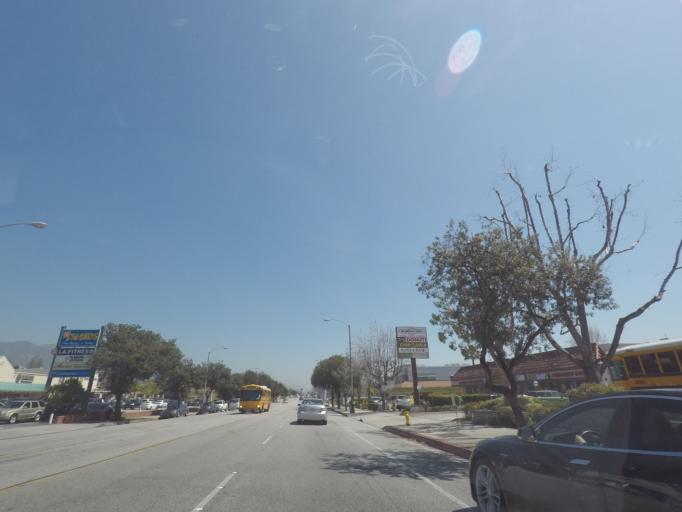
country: US
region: California
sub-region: Los Angeles County
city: East Pasadena
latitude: 34.1501
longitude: -118.0775
